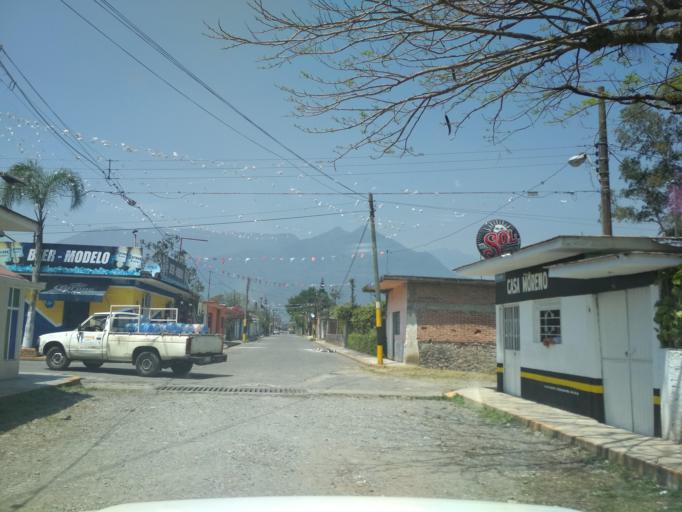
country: MX
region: Veracruz
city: Rio Blanco
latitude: 18.8326
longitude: -97.1110
